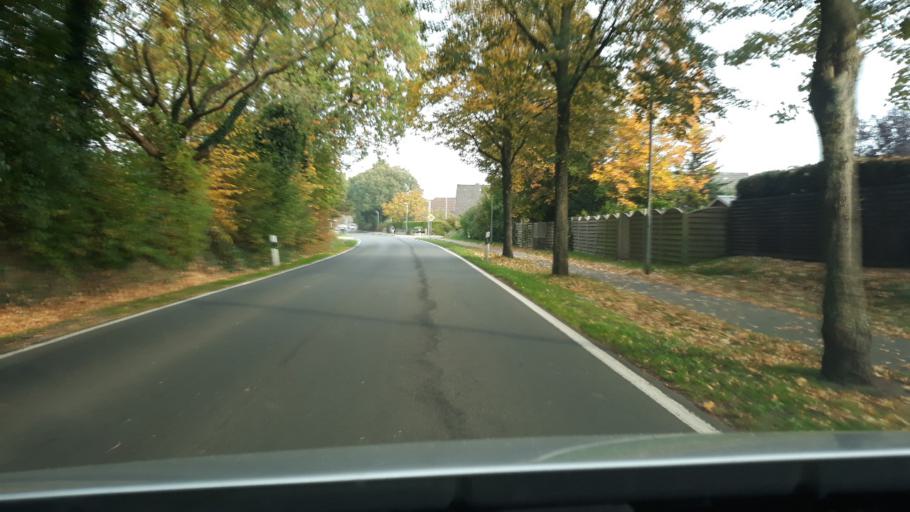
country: DE
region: Schleswig-Holstein
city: Kropp
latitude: 54.4055
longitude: 9.5109
